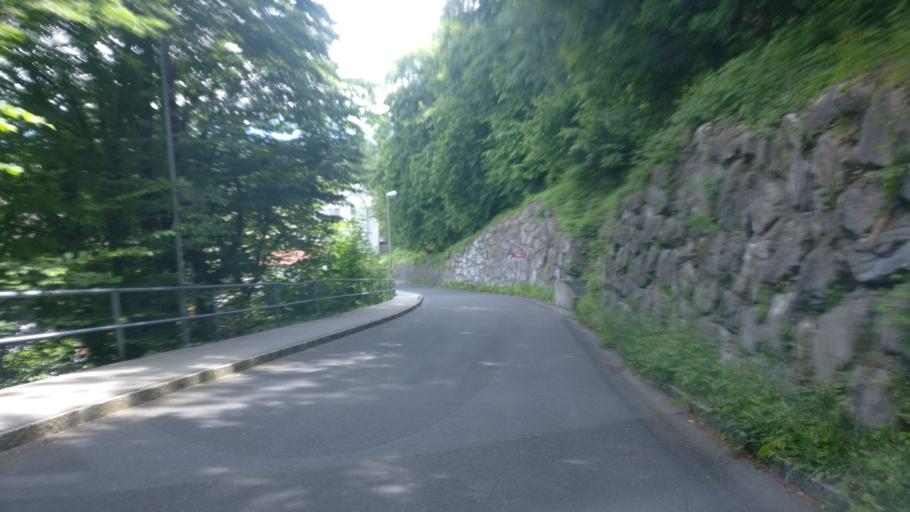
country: AT
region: Salzburg
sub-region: Politischer Bezirk Hallein
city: Hallein
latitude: 47.6773
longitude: 13.0941
